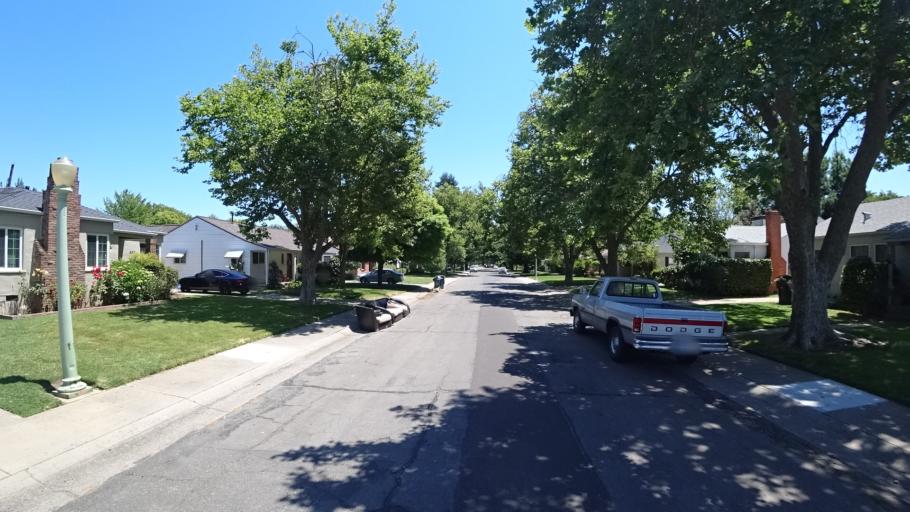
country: US
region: California
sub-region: Sacramento County
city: Sacramento
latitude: 38.5567
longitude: -121.5086
